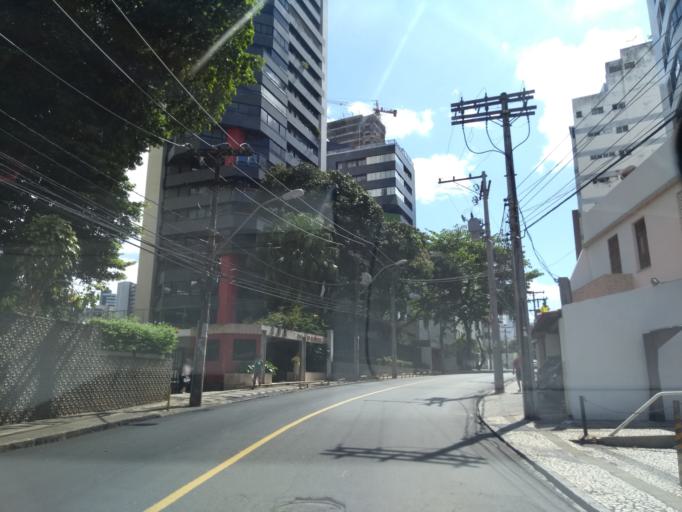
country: BR
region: Bahia
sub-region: Salvador
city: Salvador
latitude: -13.0029
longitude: -38.5263
